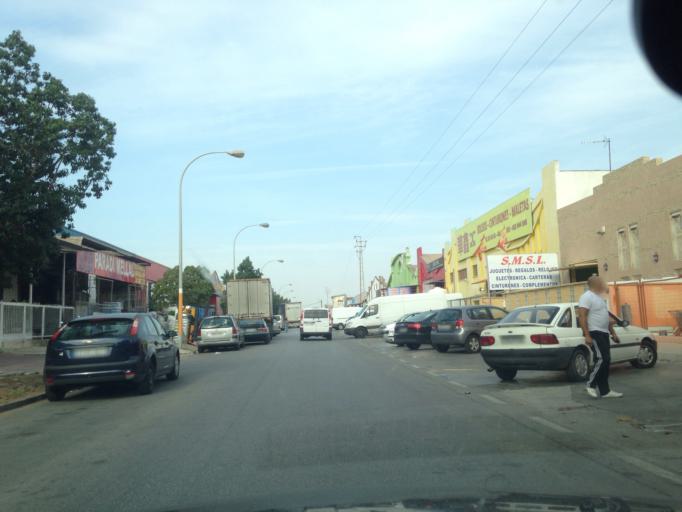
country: ES
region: Andalusia
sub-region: Provincia de Malaga
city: Malaga
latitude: 36.6894
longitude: -4.4739
